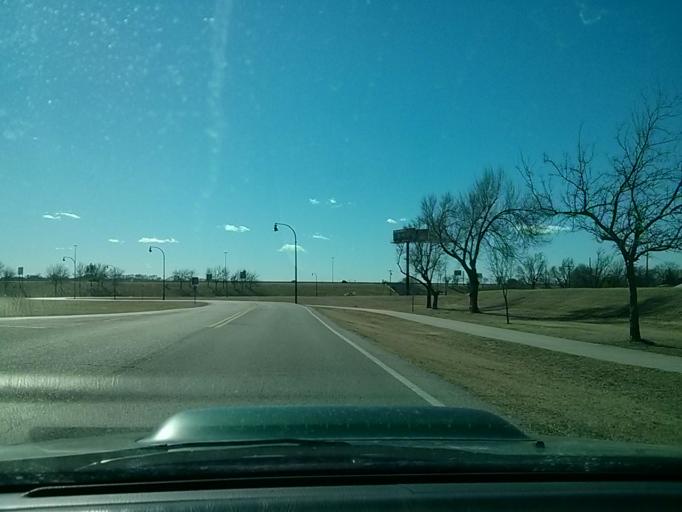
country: US
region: Oklahoma
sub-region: Tulsa County
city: Jenks
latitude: 36.0192
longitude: -95.9600
